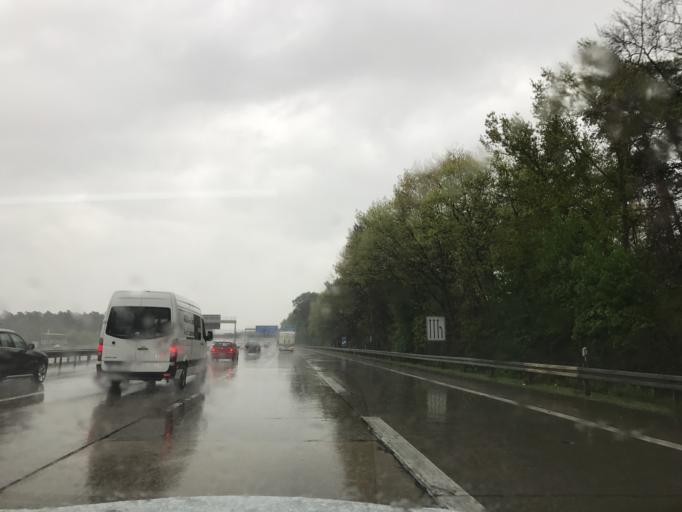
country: DE
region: Baden-Wuerttemberg
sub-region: Karlsruhe Region
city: Hockenheim
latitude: 49.3262
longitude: 8.5638
